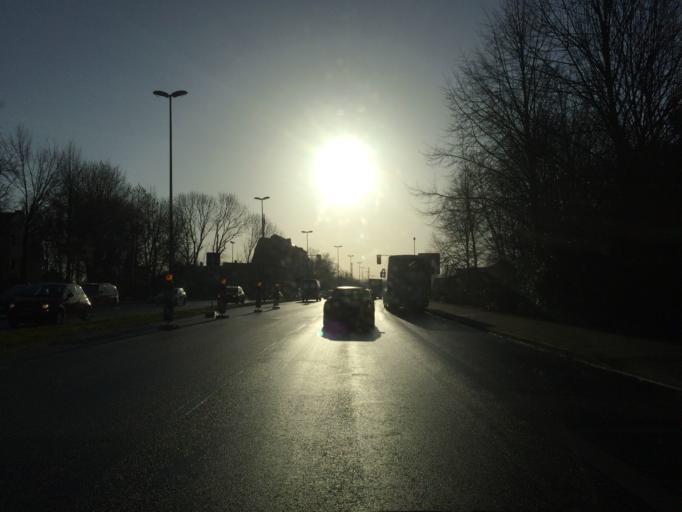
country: DE
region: North Rhine-Westphalia
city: Bochum-Hordel
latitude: 51.5393
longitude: 7.1773
